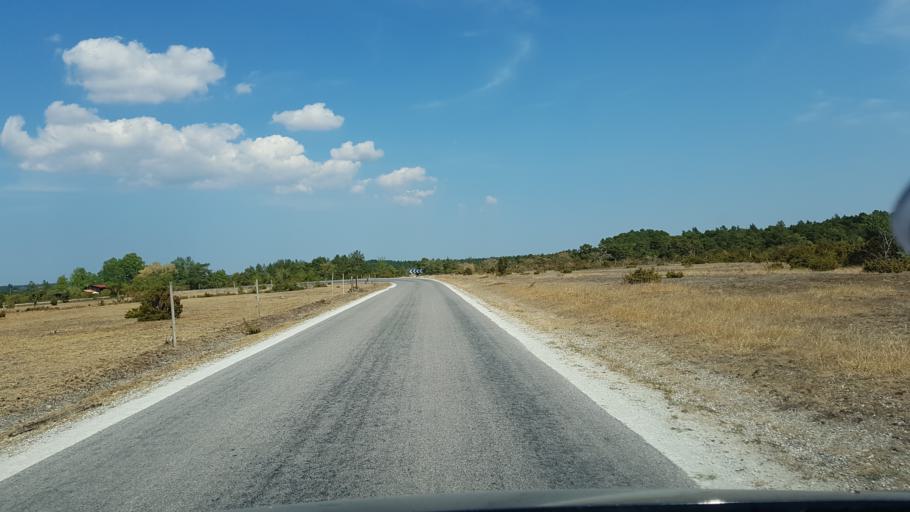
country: SE
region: Gotland
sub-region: Gotland
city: Visby
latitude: 57.6616
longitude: 18.3753
